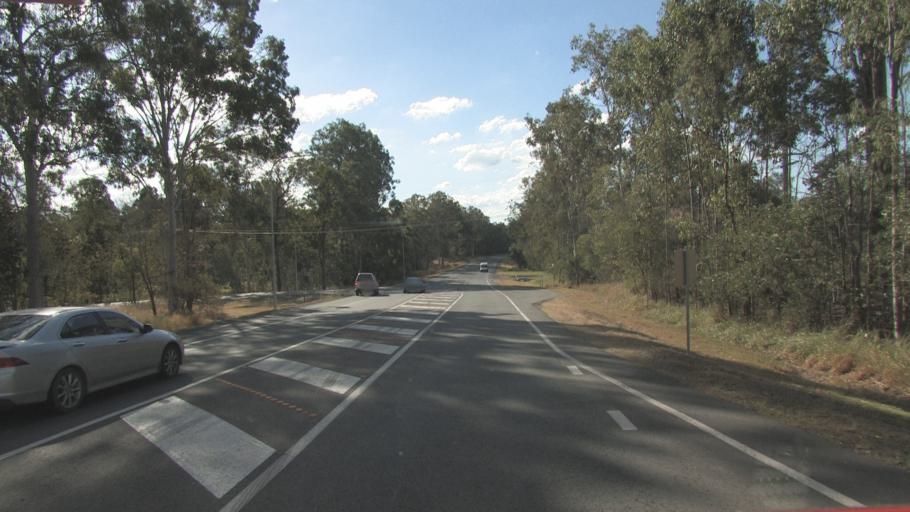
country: AU
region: Queensland
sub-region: Logan
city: North Maclean
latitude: -27.7848
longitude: 152.9806
